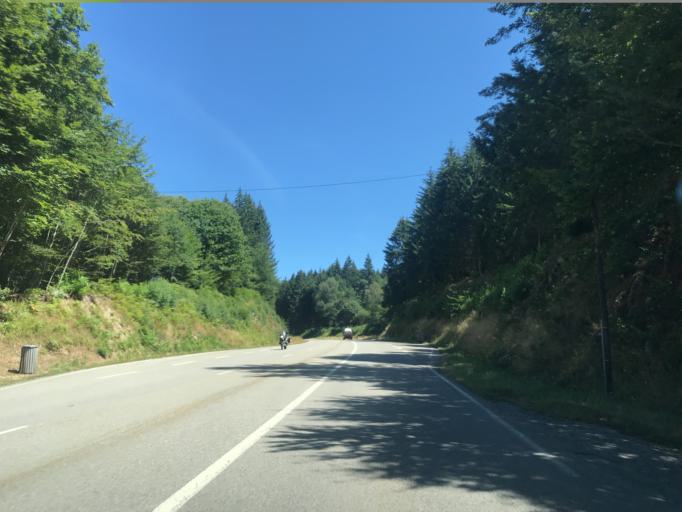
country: FR
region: Limousin
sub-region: Departement de la Correze
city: Meymac
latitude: 45.4778
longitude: 2.1882
